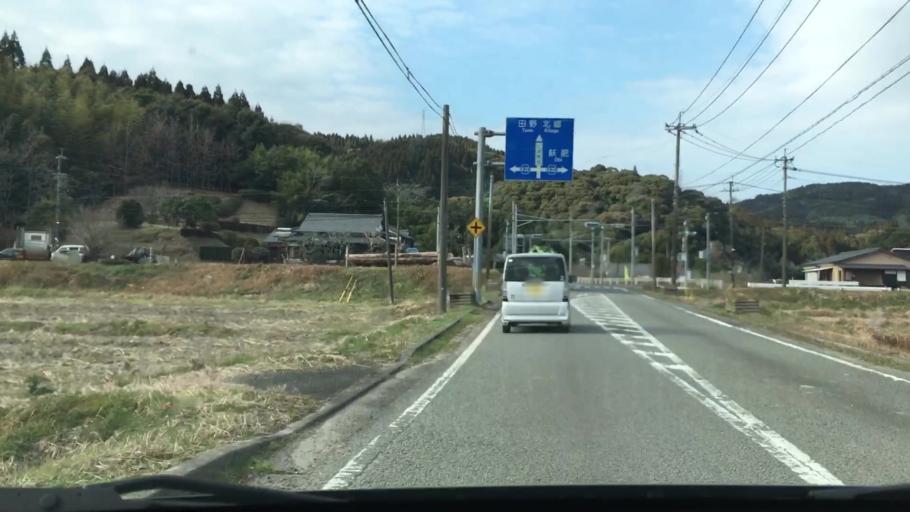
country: JP
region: Miyazaki
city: Nichinan
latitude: 31.6287
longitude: 131.3419
